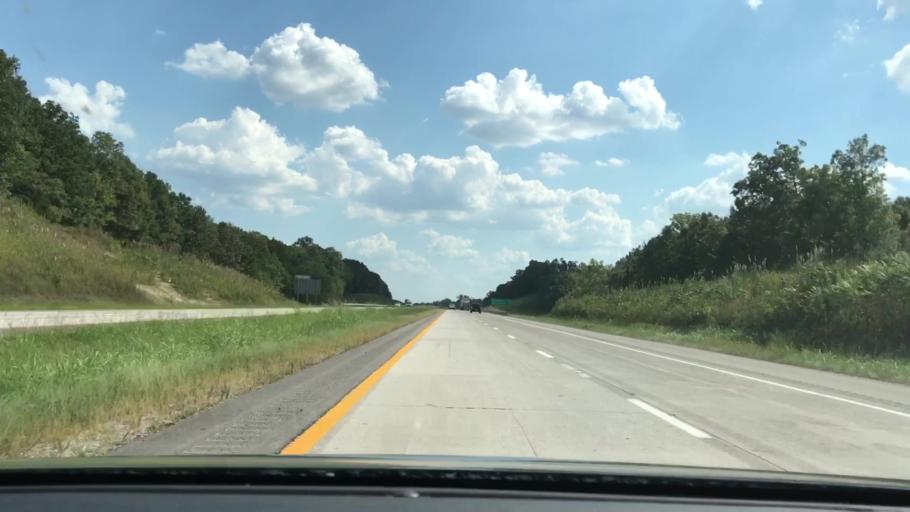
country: US
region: Kentucky
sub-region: Ohio County
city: Oak Grove
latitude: 37.3761
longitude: -86.8042
